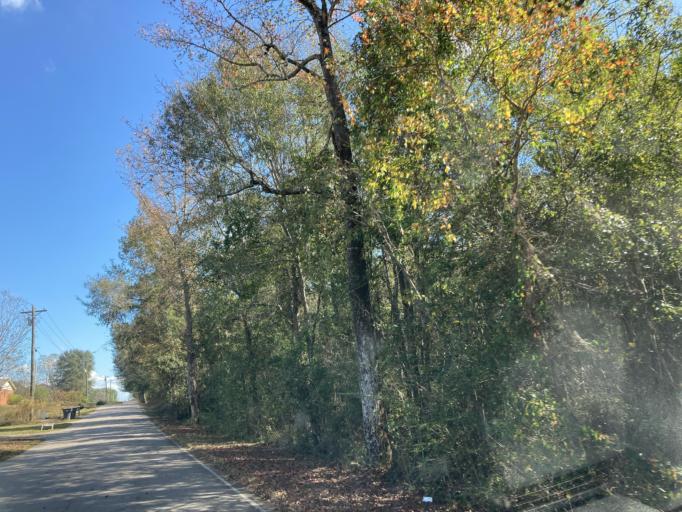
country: US
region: Mississippi
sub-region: Lamar County
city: Purvis
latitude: 31.2295
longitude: -89.4261
